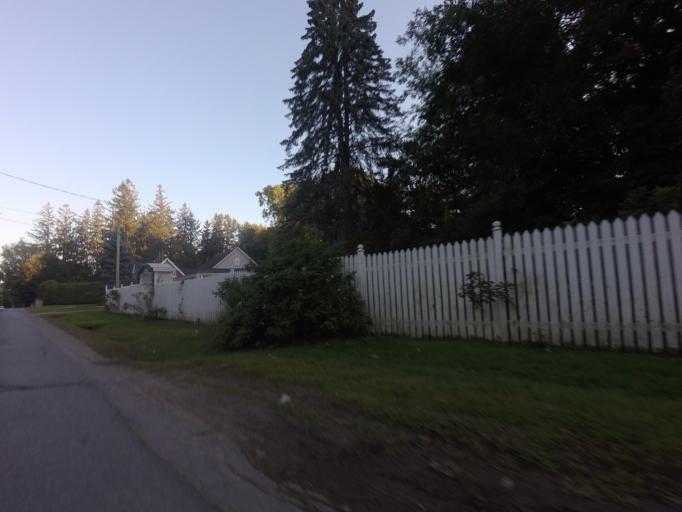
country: CA
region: Quebec
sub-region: Monteregie
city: Hudson
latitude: 45.4663
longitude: -74.1561
